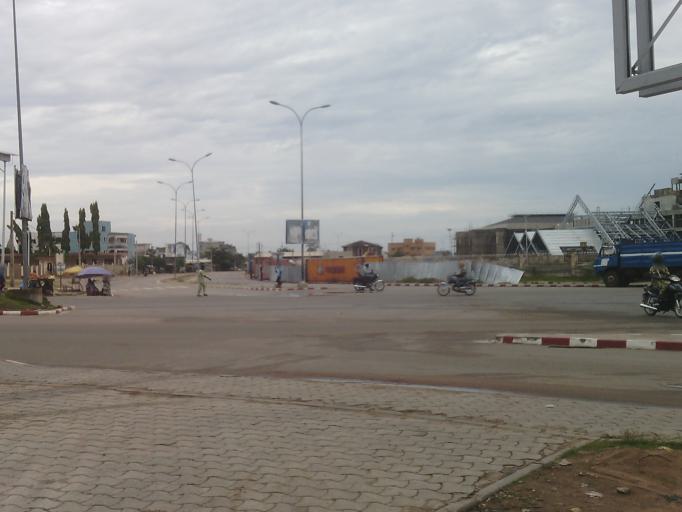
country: BJ
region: Queme
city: Porto-Novo
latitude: 6.4695
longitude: 2.6196
